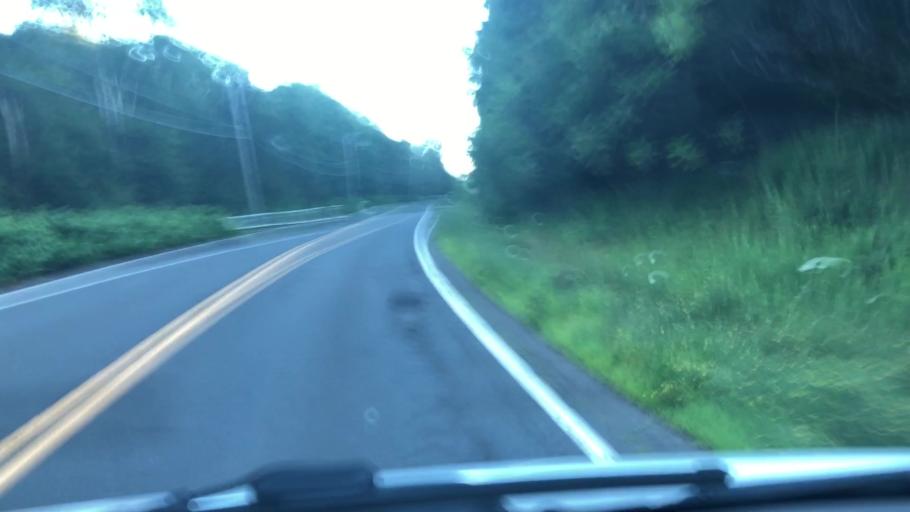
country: US
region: Massachusetts
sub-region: Hampshire County
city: Westhampton
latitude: 42.2838
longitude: -72.8329
